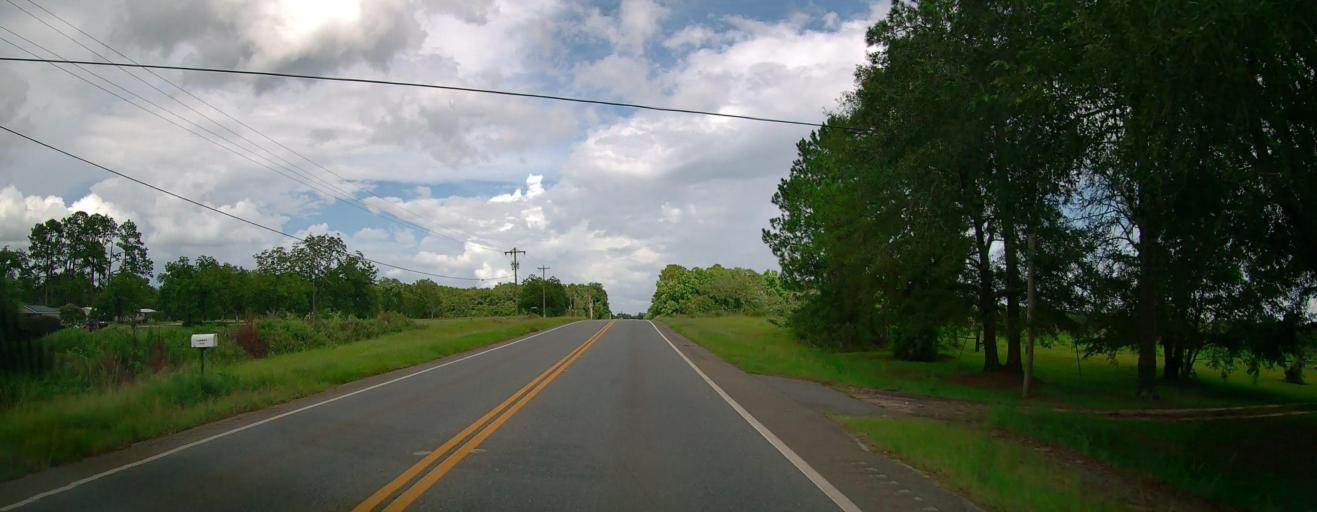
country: US
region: Georgia
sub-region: Coffee County
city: Douglas
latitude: 31.5390
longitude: -82.8828
